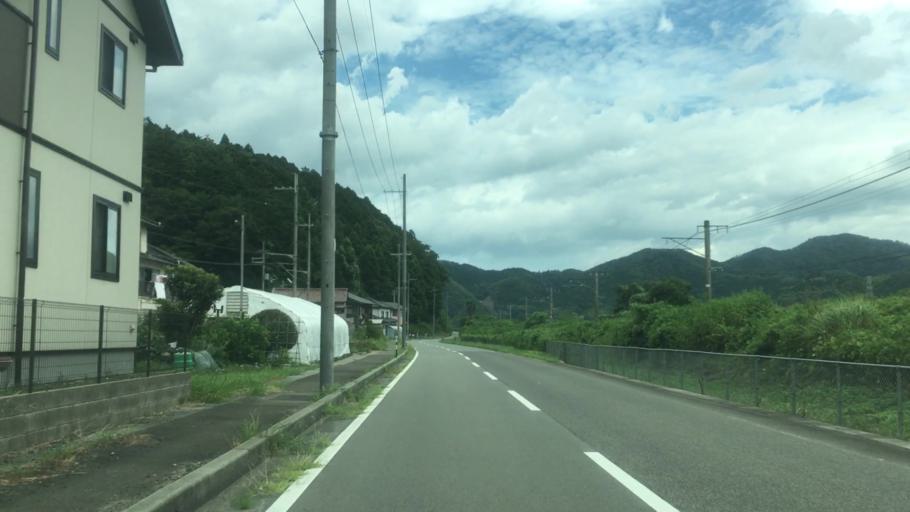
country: JP
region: Hyogo
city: Toyooka
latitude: 35.5698
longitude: 134.8042
